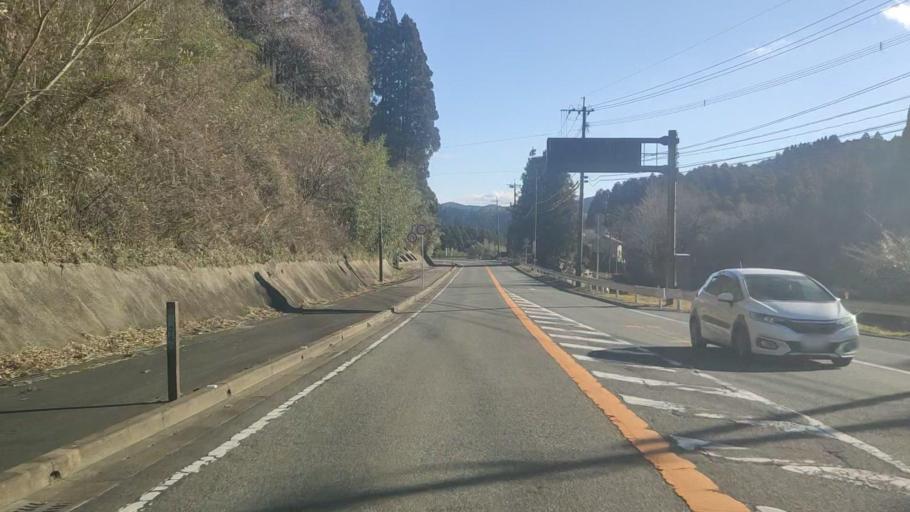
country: JP
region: Fukuoka
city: Maebaru-chuo
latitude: 33.4581
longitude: 130.2738
